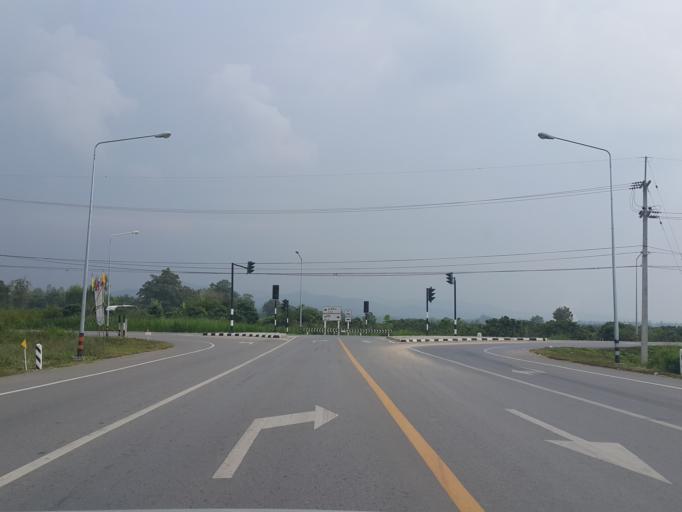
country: TH
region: Chiang Mai
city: Mae Taeng
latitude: 19.0664
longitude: 98.9596
